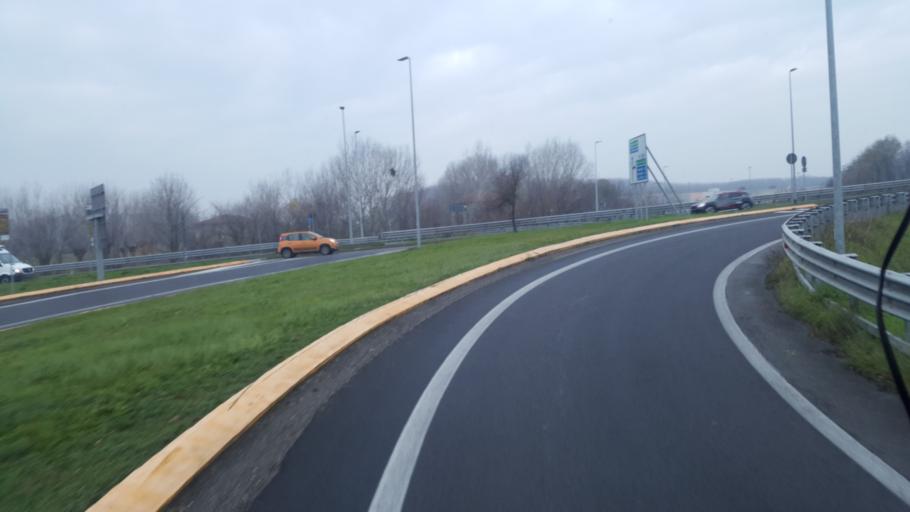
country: IT
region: Emilia-Romagna
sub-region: Provincia di Parma
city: Parma
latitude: 44.8208
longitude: 10.3277
